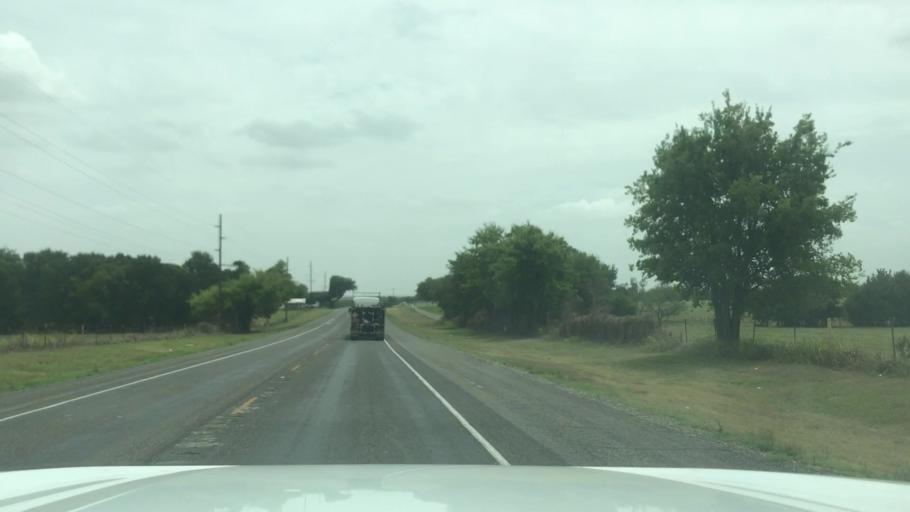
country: US
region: Texas
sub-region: Bosque County
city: Clifton
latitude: 31.7527
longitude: -97.5578
